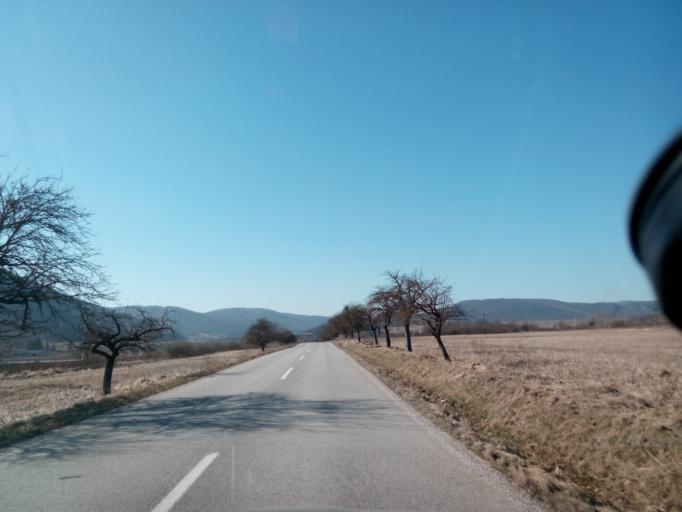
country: SK
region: Kosicky
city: Roznava
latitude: 48.5855
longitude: 20.6642
